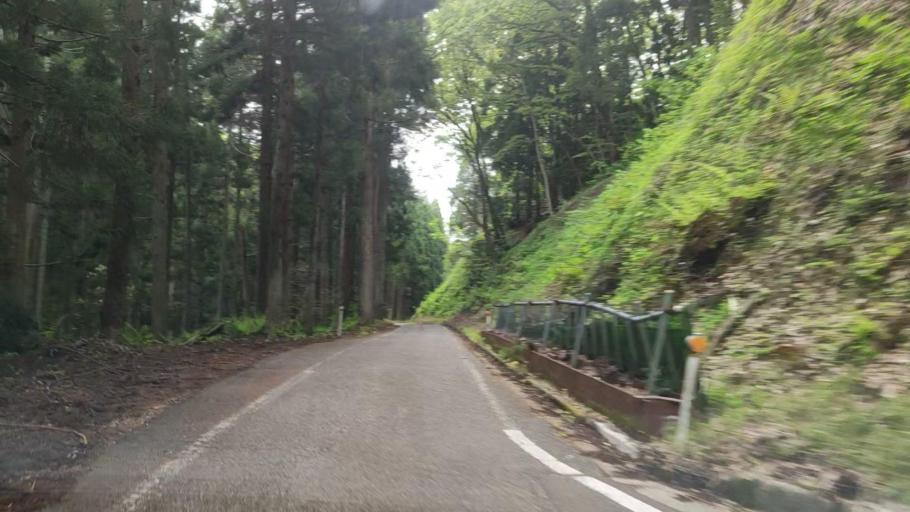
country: JP
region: Niigata
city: Kamo
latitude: 37.7173
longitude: 139.0907
